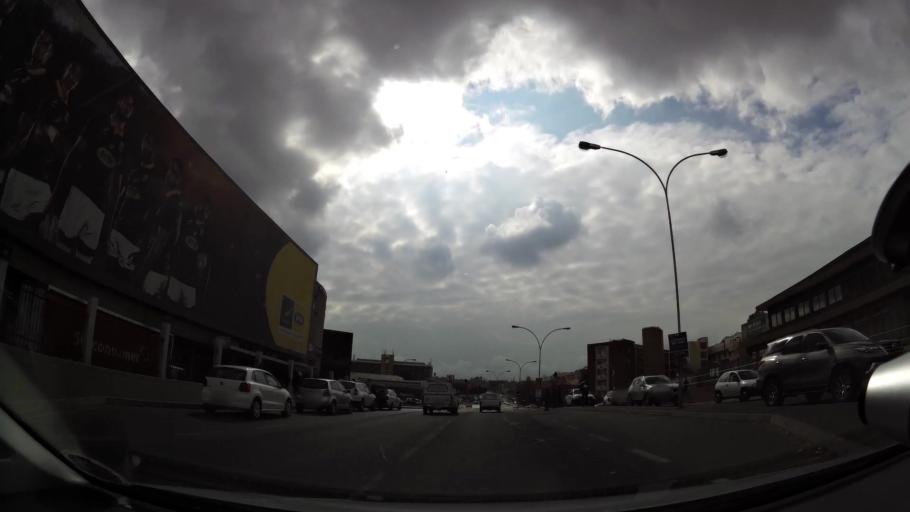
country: ZA
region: Orange Free State
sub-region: Mangaung Metropolitan Municipality
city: Bloemfontein
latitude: -29.1147
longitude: 26.2118
